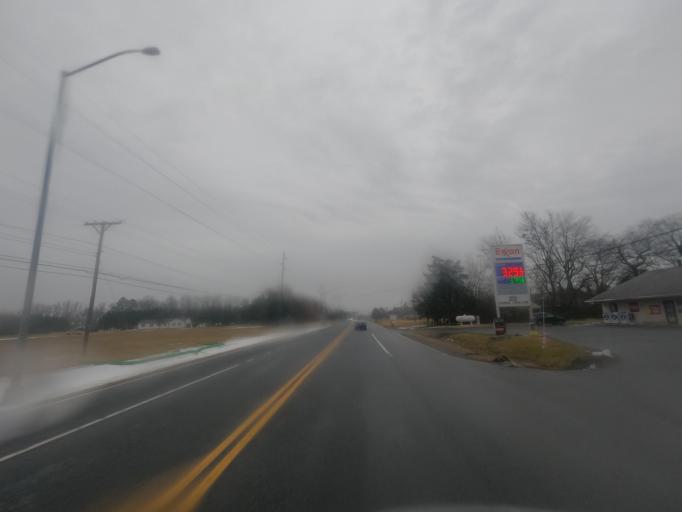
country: US
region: Maryland
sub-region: Dorchester County
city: Cambridge
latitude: 38.5786
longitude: -75.9710
